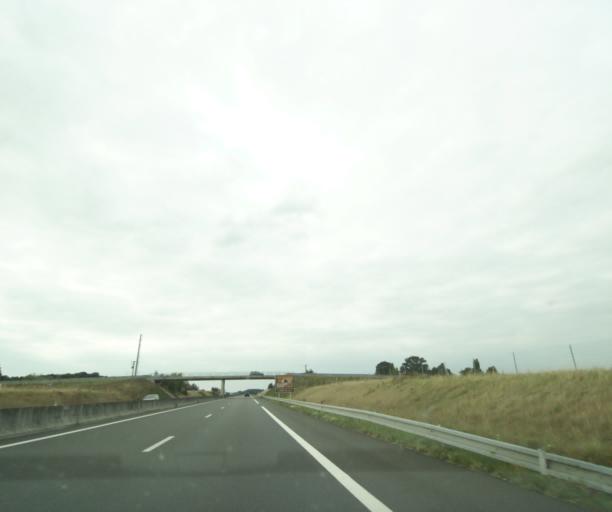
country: FR
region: Centre
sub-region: Departement d'Indre-et-Loire
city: Saint-Paterne-Racan
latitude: 47.6197
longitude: 0.5184
